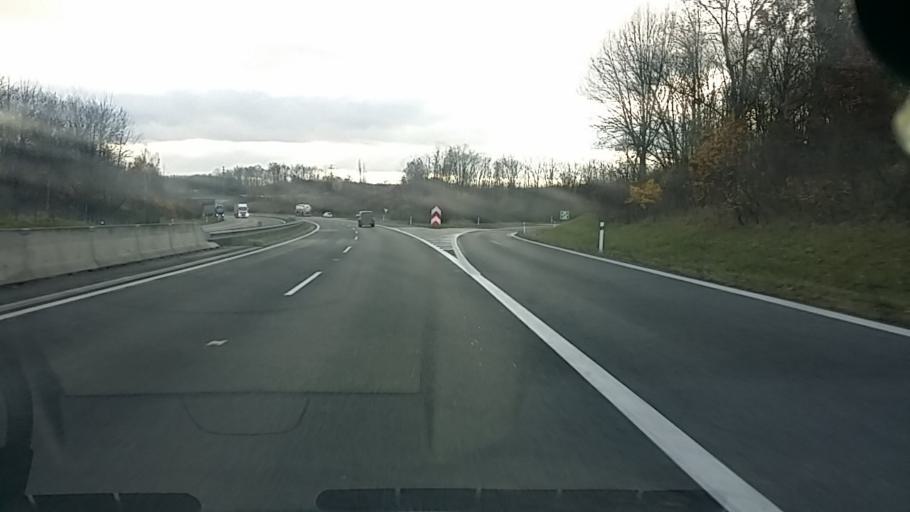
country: CZ
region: Ustecky
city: Chlumec
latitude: 50.6891
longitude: 13.9525
